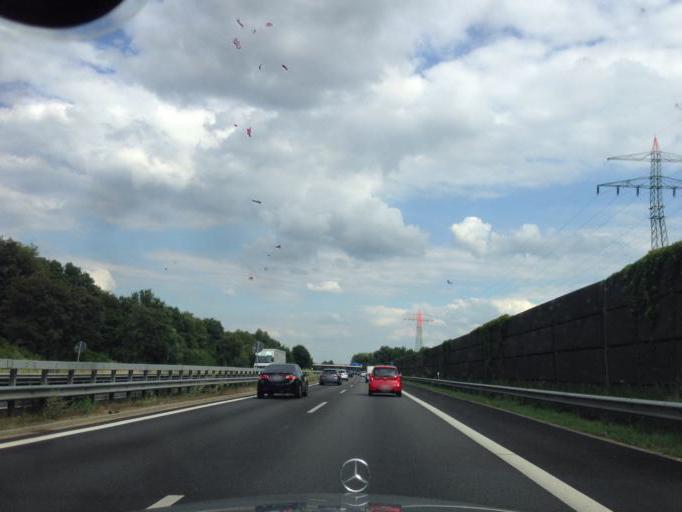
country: DE
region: Hamburg
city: Bergedorf
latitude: 53.4753
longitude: 10.1681
